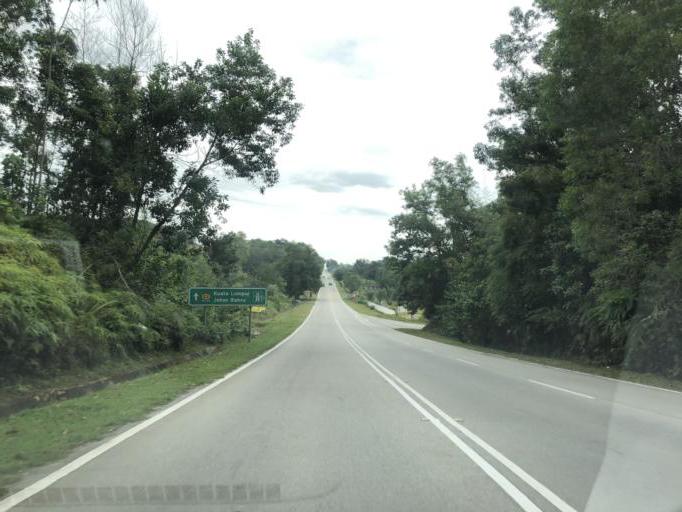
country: MY
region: Putrajaya
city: Putrajaya
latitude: 2.9252
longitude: 101.7472
